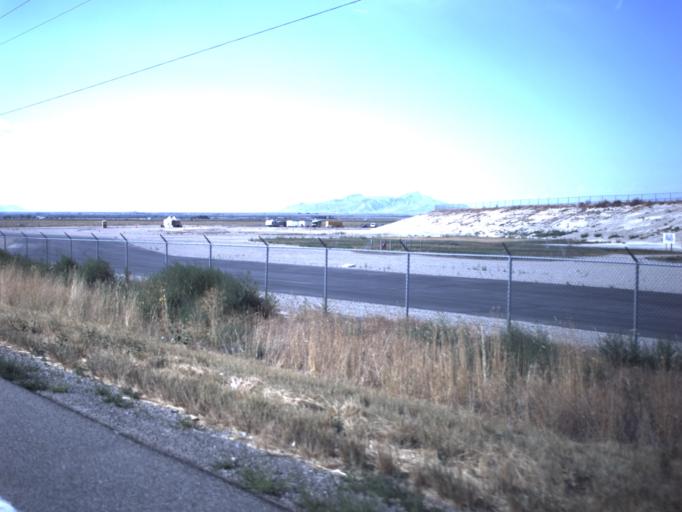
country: US
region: Utah
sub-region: Tooele County
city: Grantsville
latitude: 40.5756
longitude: -112.3870
